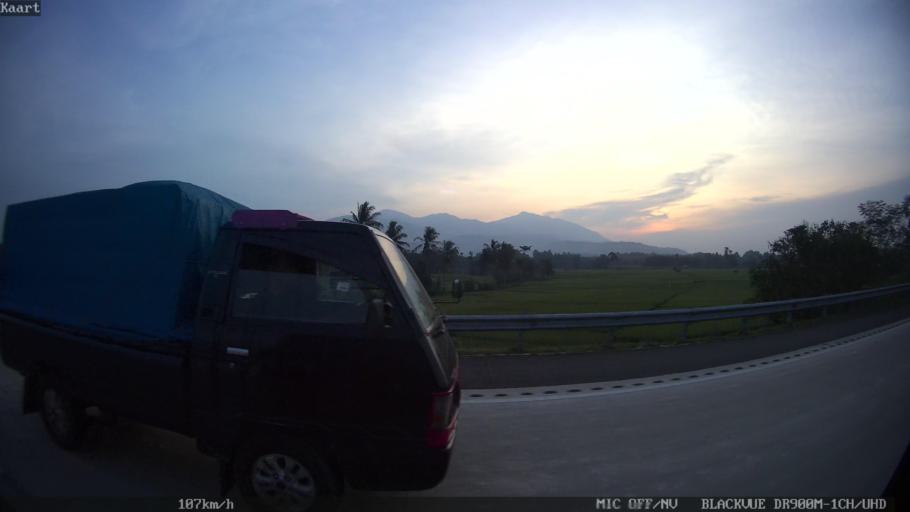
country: ID
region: Lampung
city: Penengahan
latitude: -5.7560
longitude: 105.7100
